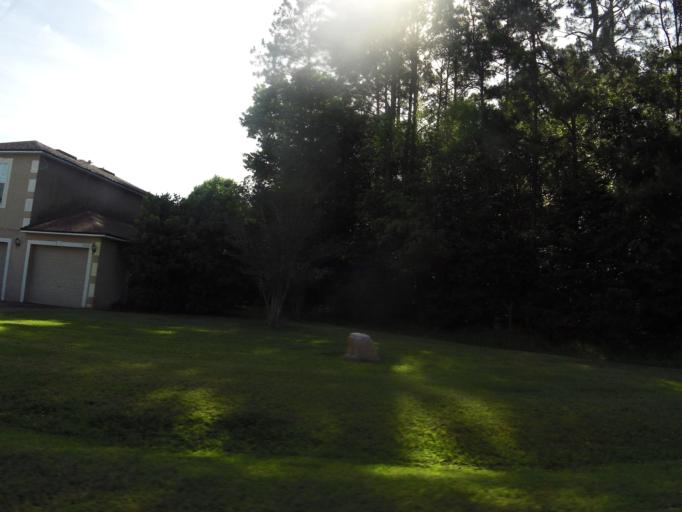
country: US
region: Florida
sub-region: Nassau County
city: Callahan
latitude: 30.5655
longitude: -81.7753
